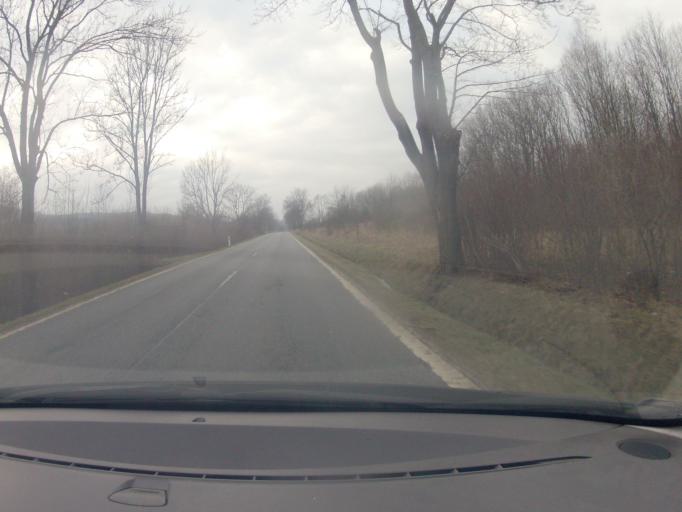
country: PL
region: Subcarpathian Voivodeship
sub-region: Powiat jasielski
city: Nowy Zmigrod
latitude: 49.5639
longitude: 21.5958
